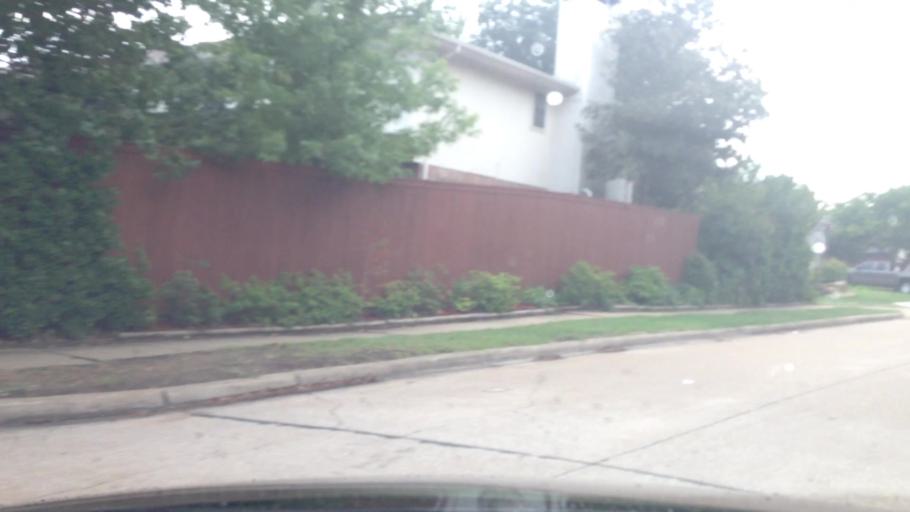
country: US
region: Texas
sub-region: Denton County
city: Lewisville
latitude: 33.0166
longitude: -97.0370
